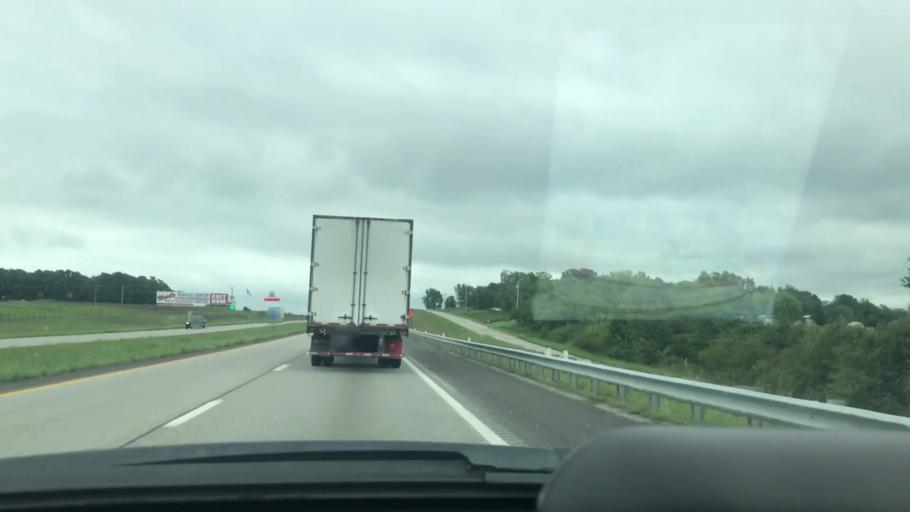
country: US
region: Missouri
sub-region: Greene County
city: Republic
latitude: 37.1845
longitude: -93.5795
